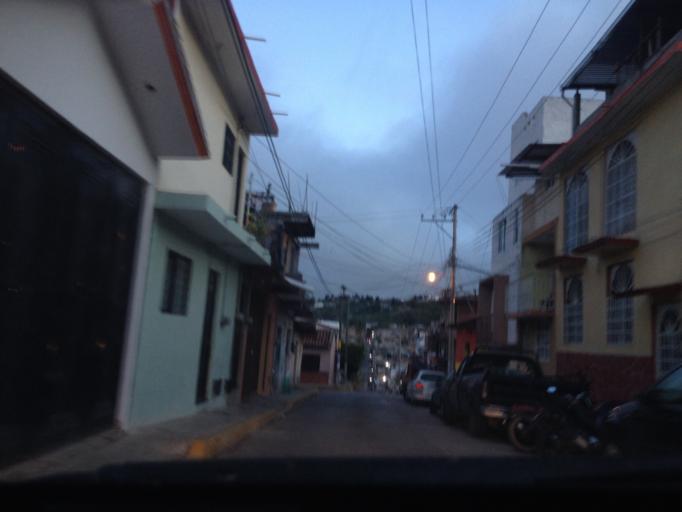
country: MX
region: Guerrero
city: Chilpancingo de los Bravos
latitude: 17.5580
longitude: -99.5002
